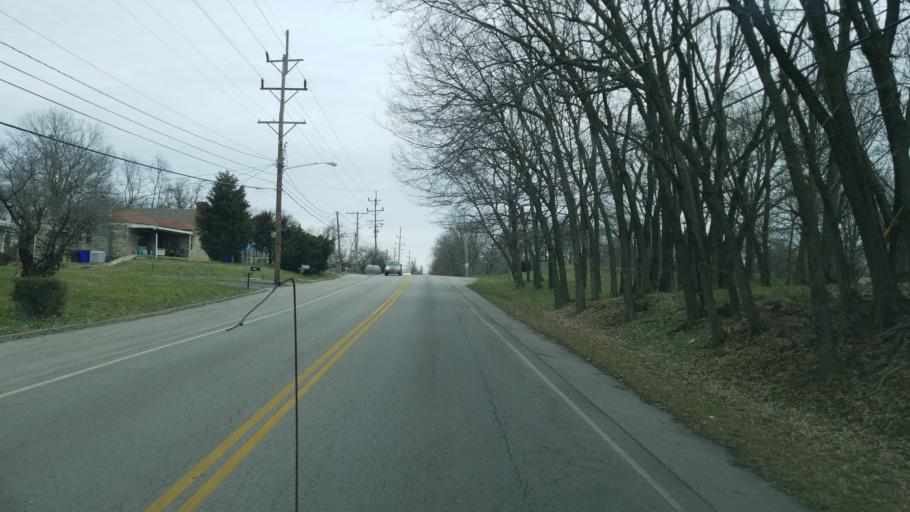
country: US
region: Kentucky
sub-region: Fayette County
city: Lexington-Fayette
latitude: 38.0669
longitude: -84.4676
